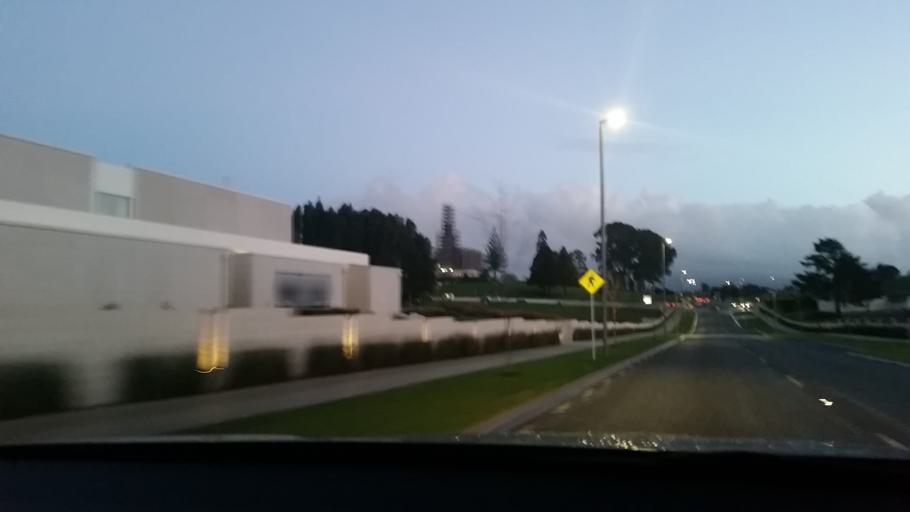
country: NZ
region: Waikato
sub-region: Hamilton City
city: Hamilton
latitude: -37.8227
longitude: 175.2257
